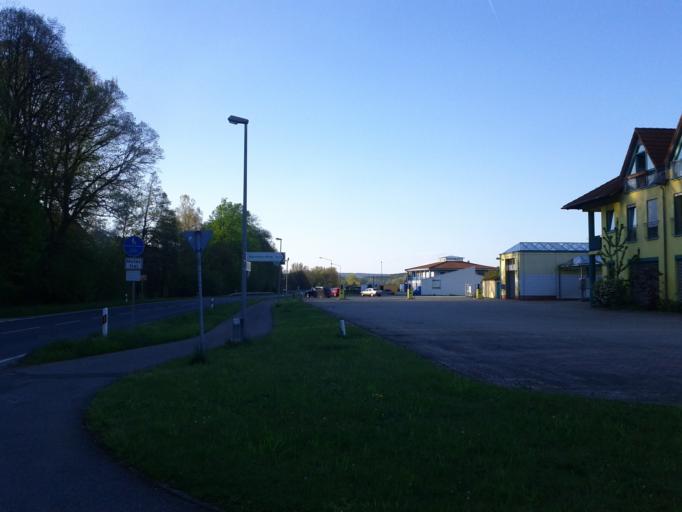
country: DE
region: Bavaria
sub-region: Upper Franconia
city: Weismain
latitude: 50.0916
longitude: 11.2386
